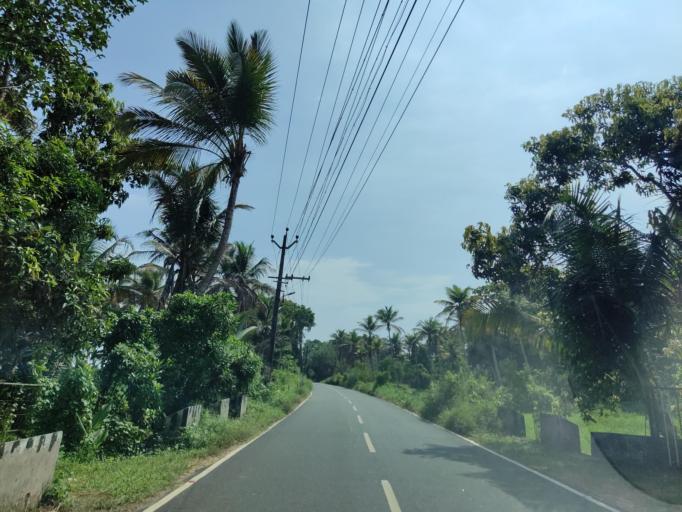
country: IN
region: Kerala
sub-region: Alappuzha
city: Mavelikara
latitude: 9.3276
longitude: 76.4738
